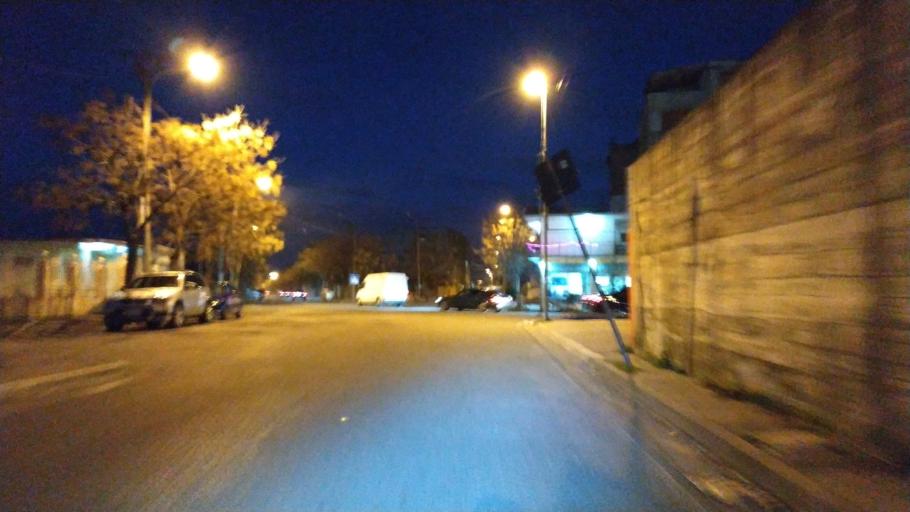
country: AL
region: Shkoder
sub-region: Rrethi i Shkodres
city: Shkoder
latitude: 42.0579
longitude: 19.5005
